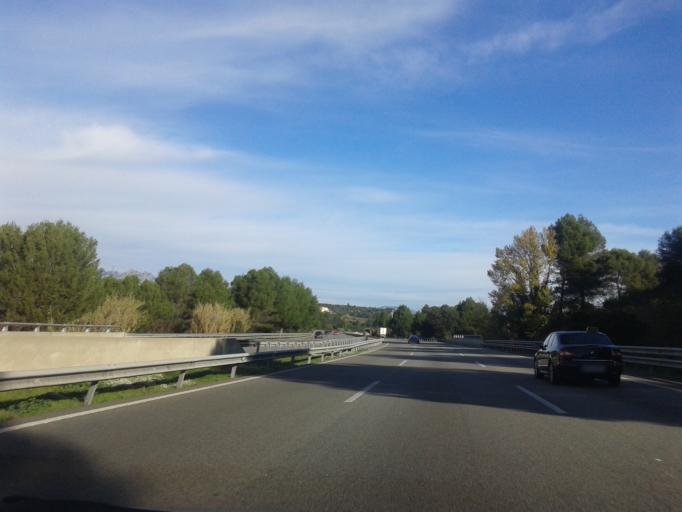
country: ES
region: Catalonia
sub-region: Provincia de Barcelona
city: Gelida
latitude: 41.4324
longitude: 1.8392
